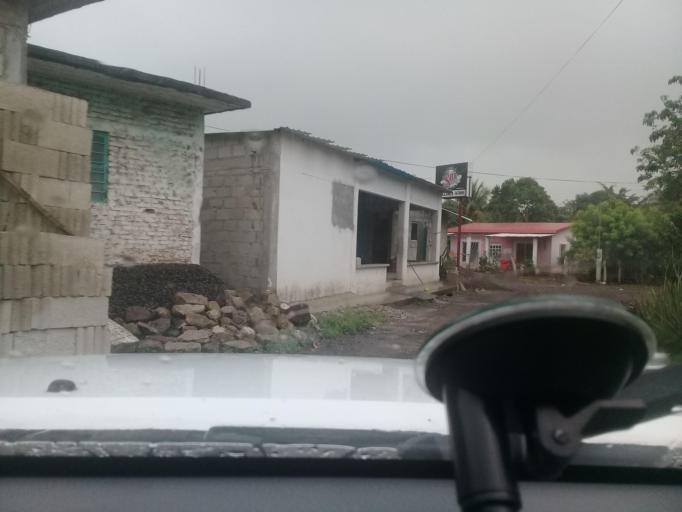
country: MX
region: Veracruz
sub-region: Puente Nacional
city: Chichicaxtle
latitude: 19.3323
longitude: -96.4242
